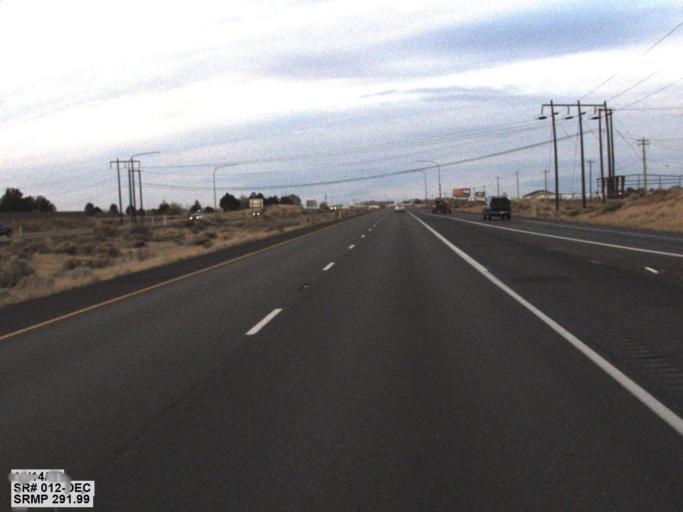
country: US
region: Washington
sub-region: Franklin County
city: Pasco
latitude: 46.2437
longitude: -119.0627
